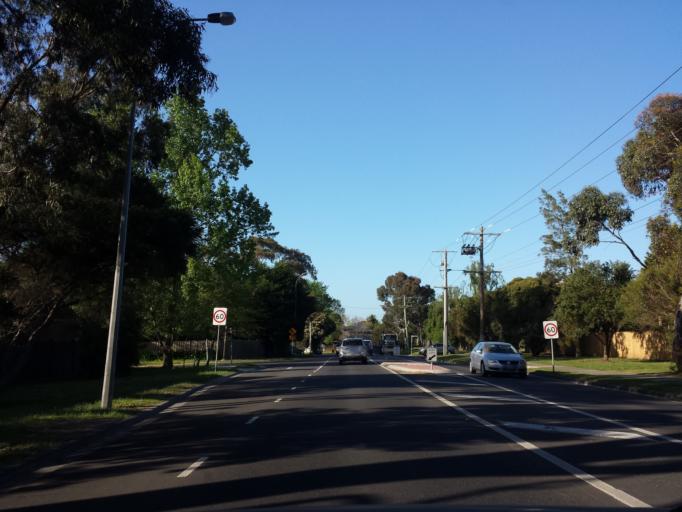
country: AU
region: Victoria
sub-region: Casey
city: Berwick
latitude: -38.0220
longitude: 145.3456
